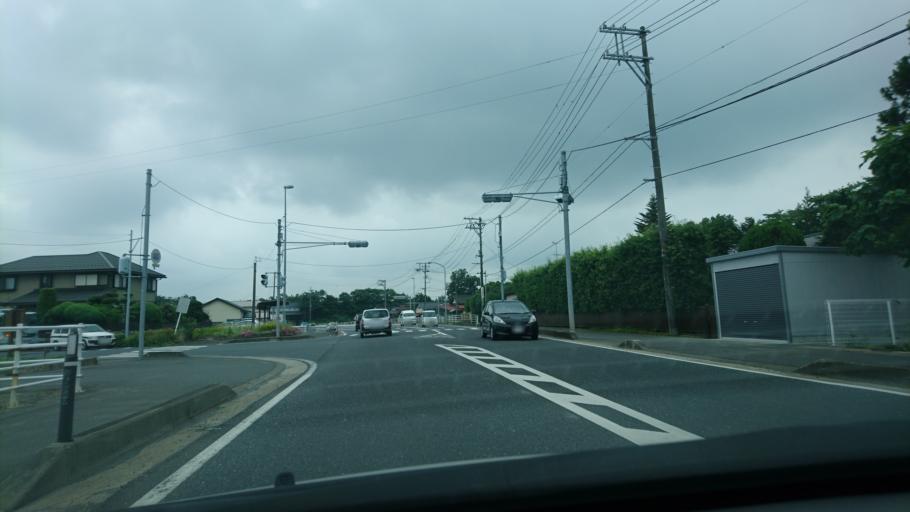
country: JP
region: Miyagi
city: Furukawa
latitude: 38.5961
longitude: 140.9326
